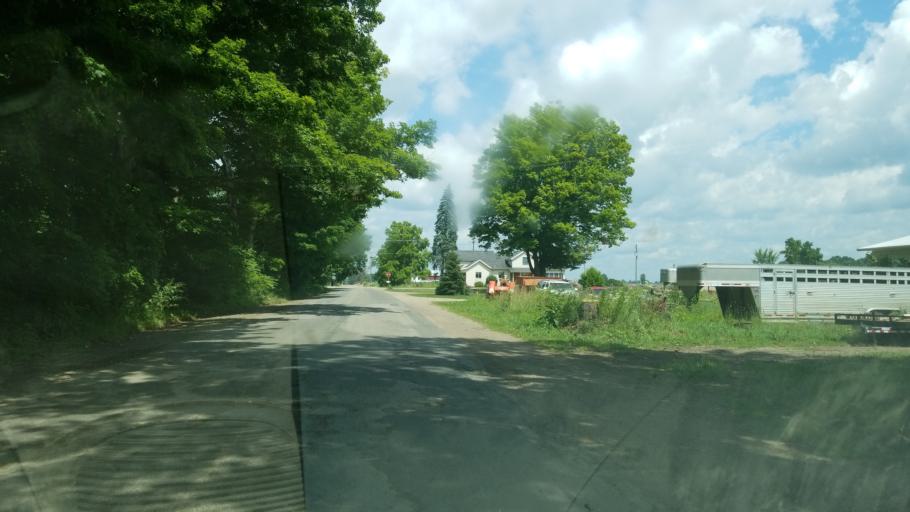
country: US
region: Michigan
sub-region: Mecosta County
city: Canadian Lakes
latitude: 43.5409
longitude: -85.3922
